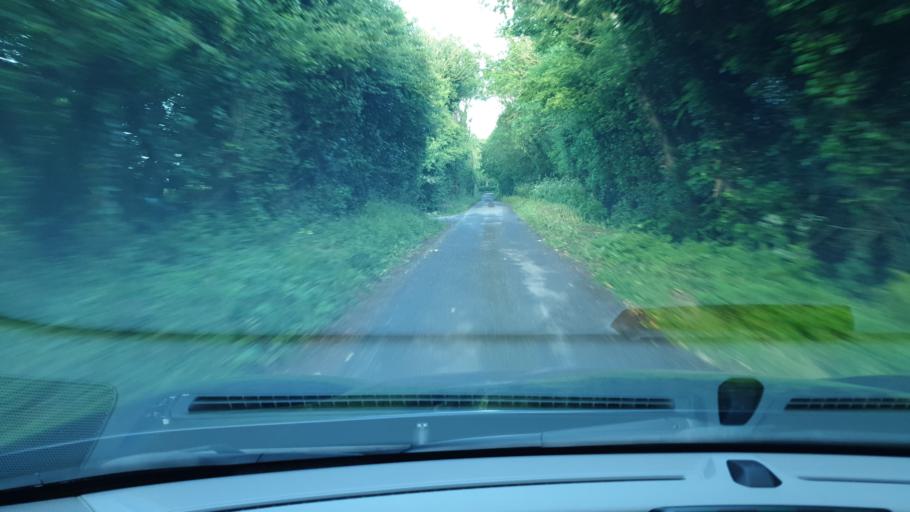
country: IE
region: Leinster
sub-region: An Mhi
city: Ashbourne
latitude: 53.4764
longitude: -6.3401
